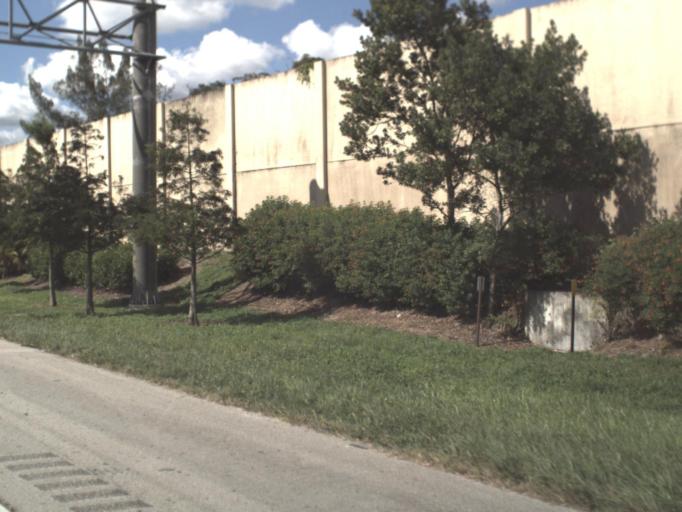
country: US
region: Florida
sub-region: Broward County
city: Parkland
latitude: 26.3010
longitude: -80.2292
